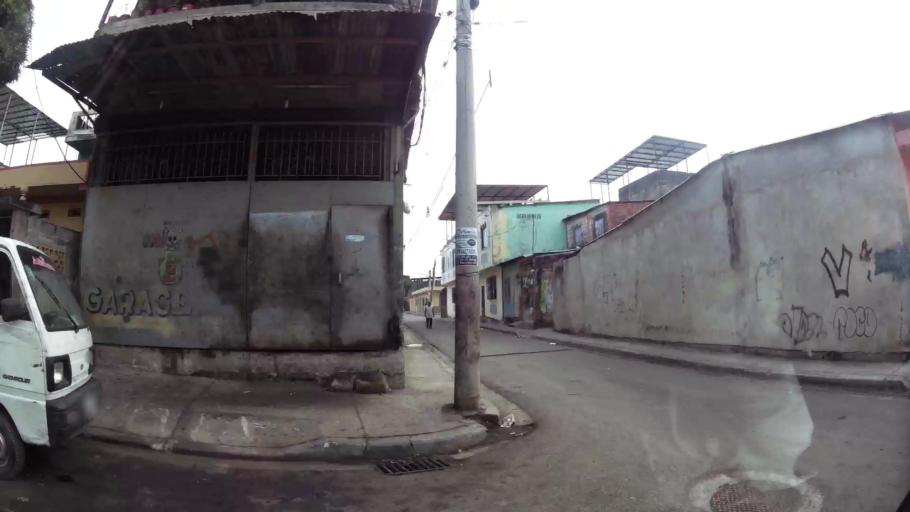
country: EC
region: Guayas
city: Guayaquil
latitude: -2.2581
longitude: -79.8876
